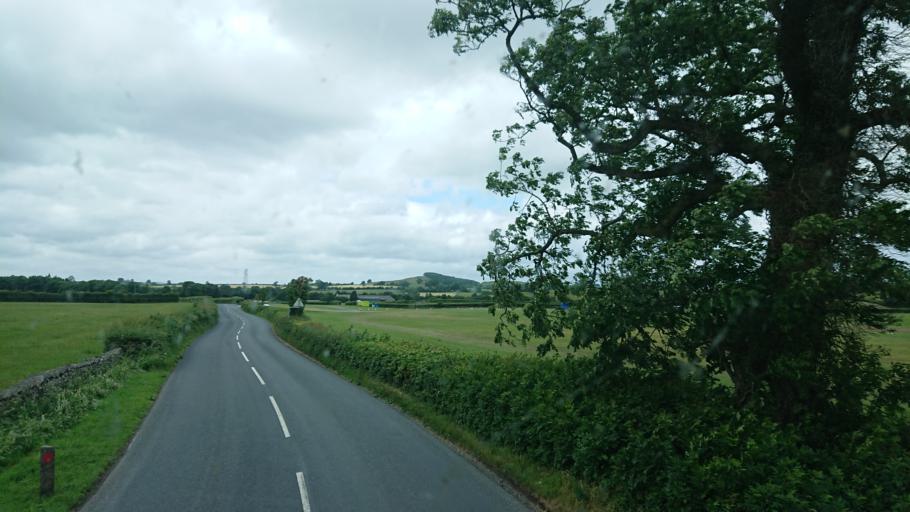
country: GB
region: England
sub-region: Cumbria
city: Milnthorpe
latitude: 54.2457
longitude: -2.7233
